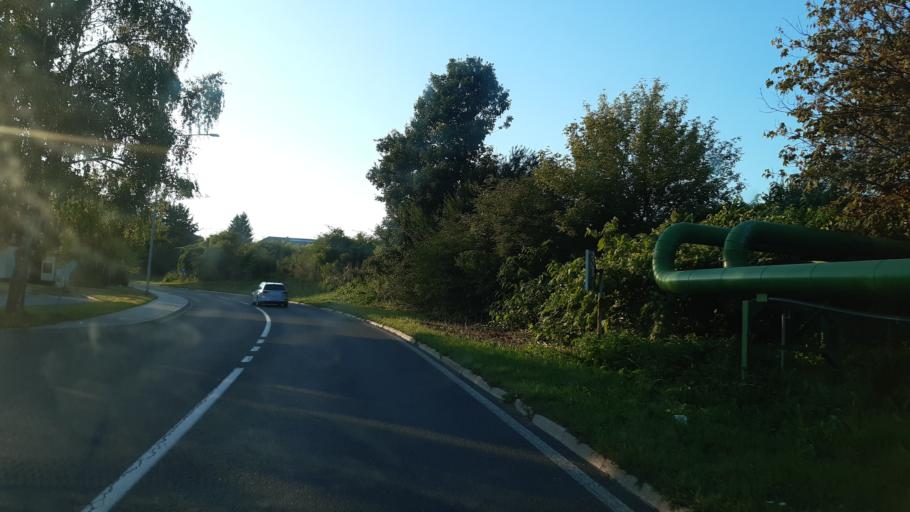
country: SI
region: Kocevje
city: Kocevje
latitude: 45.6425
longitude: 14.8619
